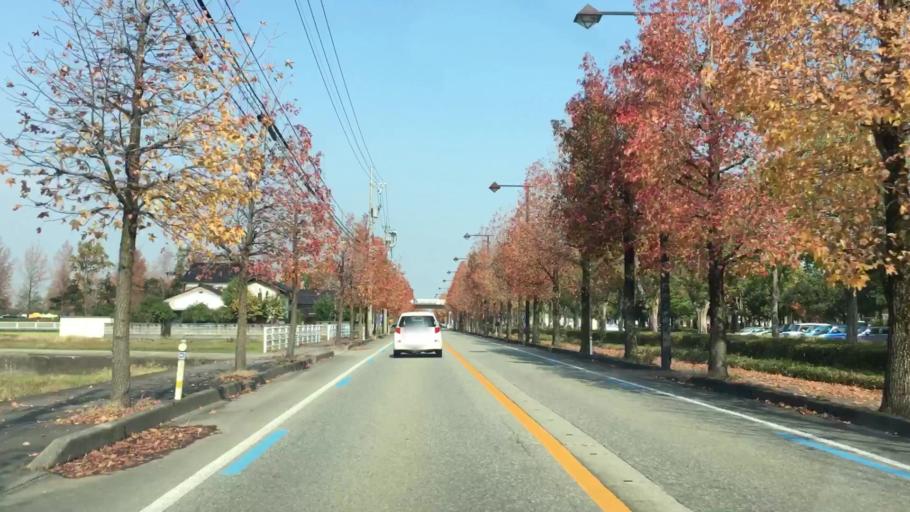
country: JP
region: Toyama
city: Toyama-shi
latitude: 36.6246
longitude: 137.1934
